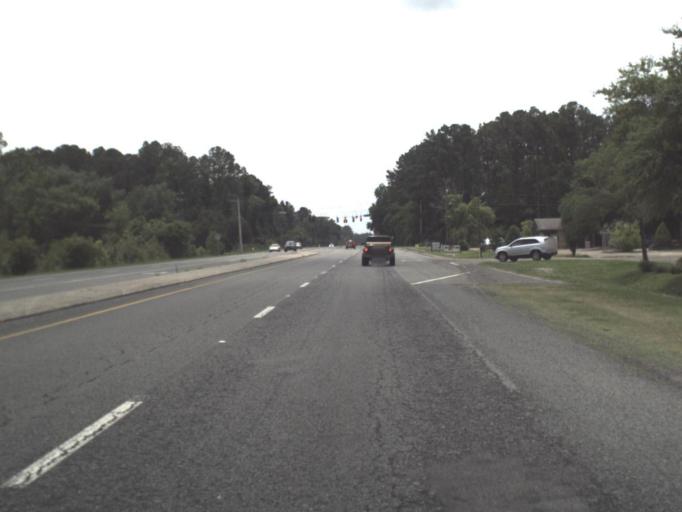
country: US
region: Florida
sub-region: Nassau County
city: Nassau Village-Ratliff
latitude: 30.5127
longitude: -81.7939
